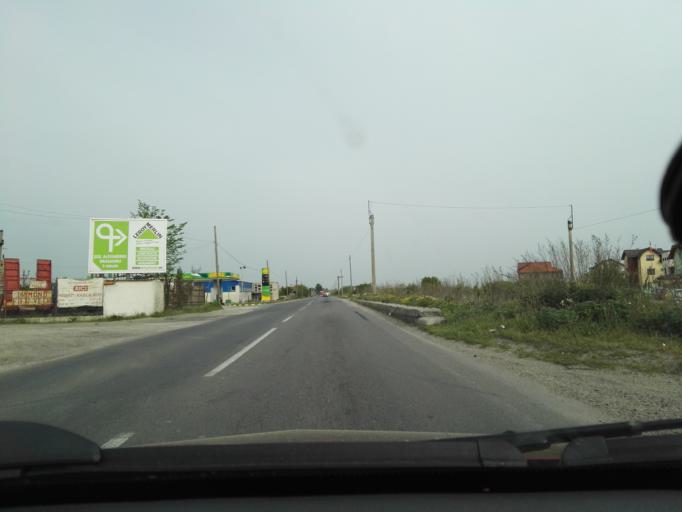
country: RO
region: Ilfov
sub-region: Comuna Magurele
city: Varteju
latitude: 44.3779
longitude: 26.0018
